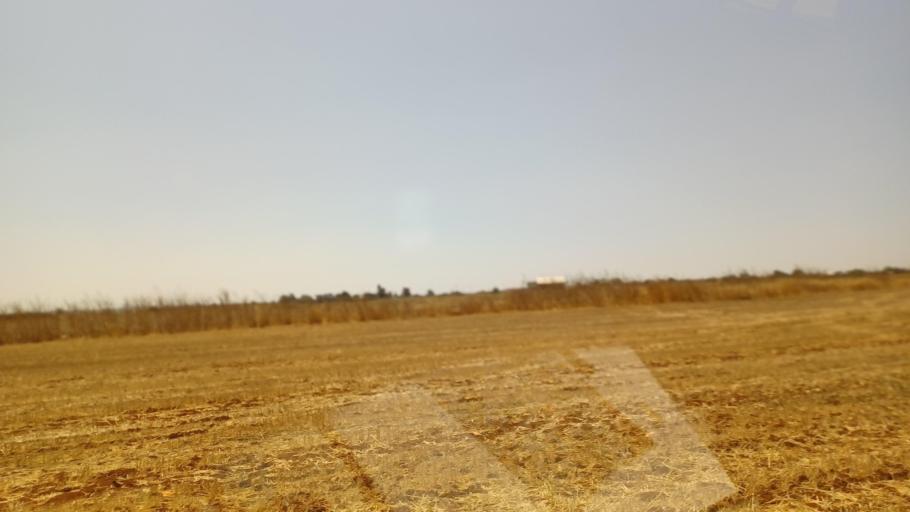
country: CY
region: Ammochostos
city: Avgorou
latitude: 35.0272
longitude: 33.8138
